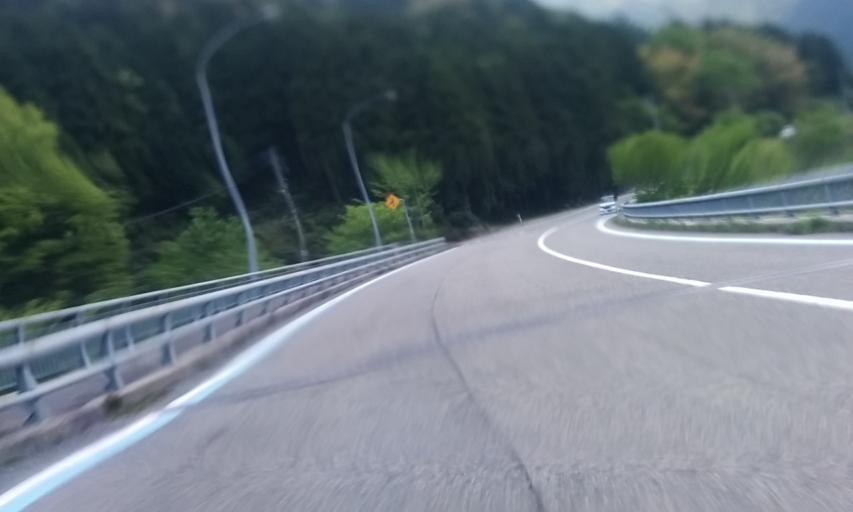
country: JP
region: Ehime
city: Saijo
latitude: 33.8333
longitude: 133.2282
